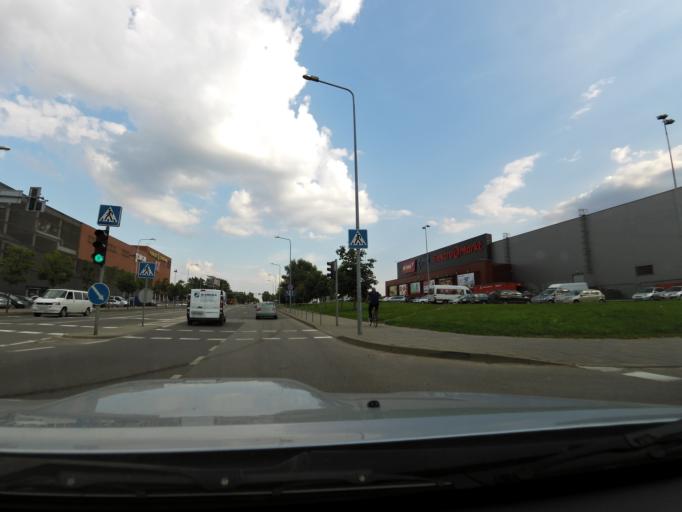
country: LT
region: Siauliu apskritis
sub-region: Siauliai
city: Siauliai
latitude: 55.9077
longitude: 23.2582
